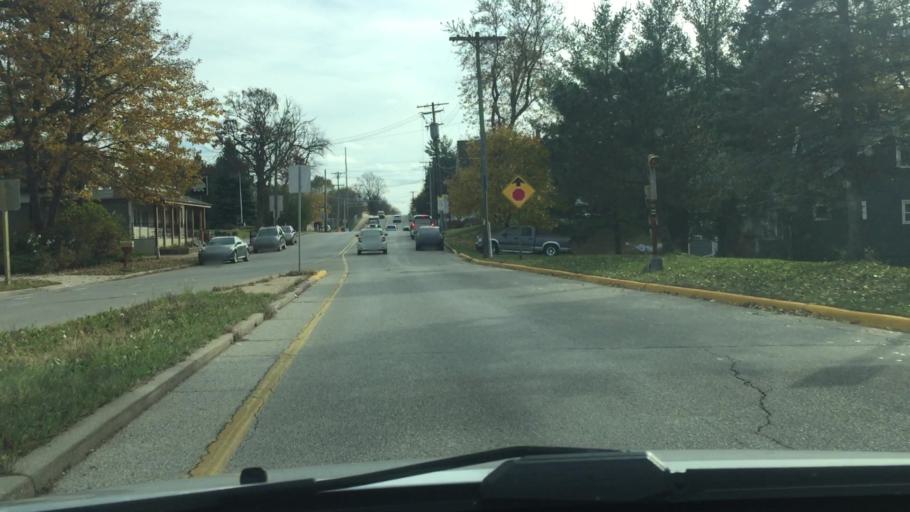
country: US
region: Wisconsin
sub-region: Waukesha County
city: Nashotah
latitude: 43.1009
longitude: -88.4030
